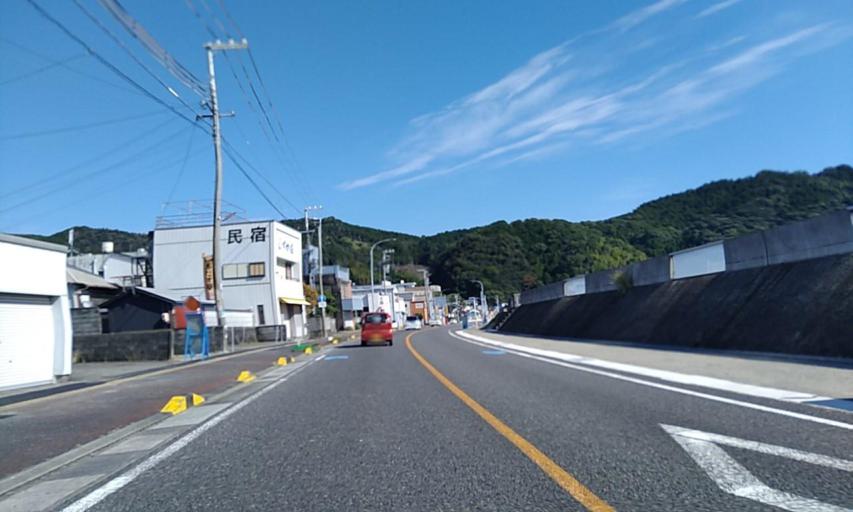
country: JP
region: Wakayama
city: Shingu
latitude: 33.8898
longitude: 136.1042
